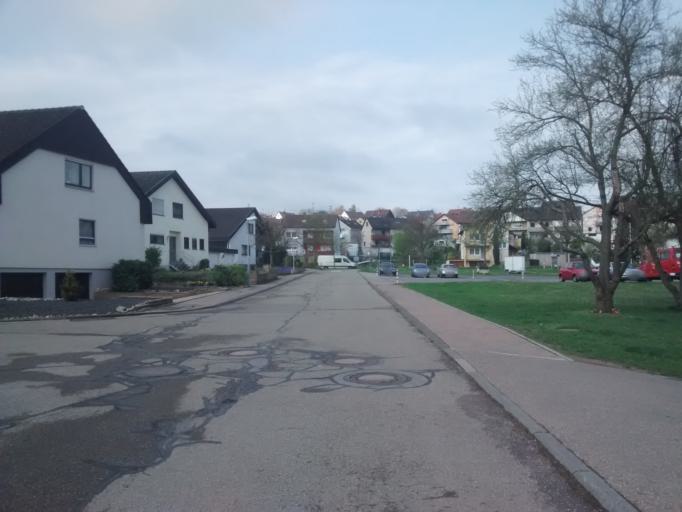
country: DE
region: Baden-Wuerttemberg
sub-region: Regierungsbezirk Stuttgart
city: Cleebronn
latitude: 49.0483
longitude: 9.0421
